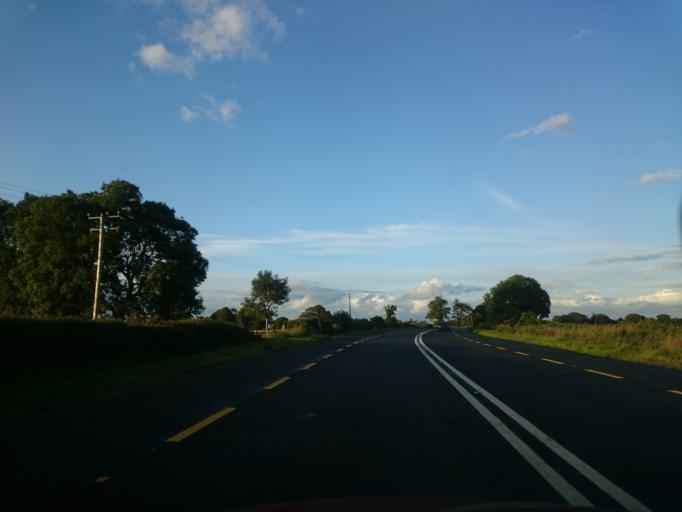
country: IE
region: Leinster
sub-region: Loch Garman
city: Ballinroad
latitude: 52.6286
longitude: -6.3945
